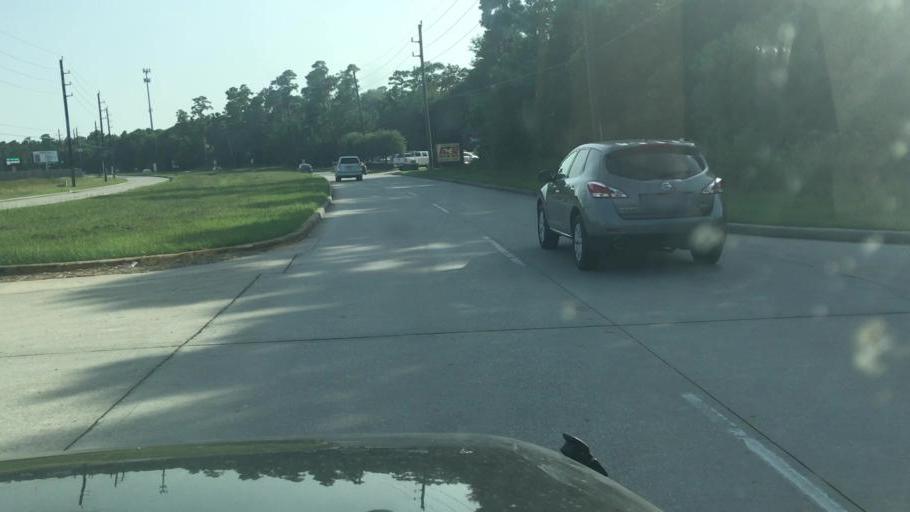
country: US
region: Texas
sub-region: Harris County
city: Atascocita
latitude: 29.9778
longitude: -95.1692
